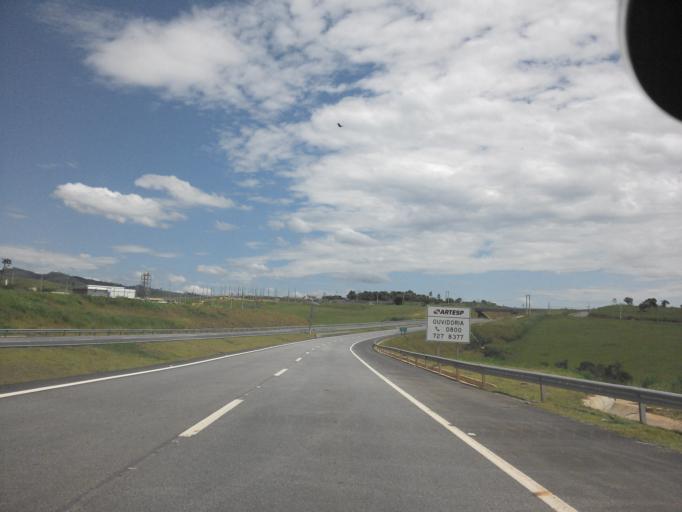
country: BR
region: Sao Paulo
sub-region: Taubate
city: Taubate
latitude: -23.0910
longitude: -45.5705
